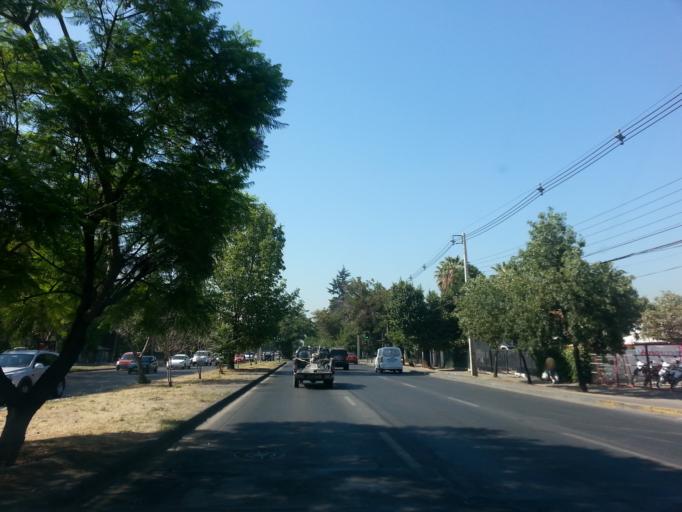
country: CL
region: Santiago Metropolitan
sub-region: Provincia de Santiago
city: Villa Presidente Frei, Nunoa, Santiago, Chile
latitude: -33.4405
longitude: -70.5731
